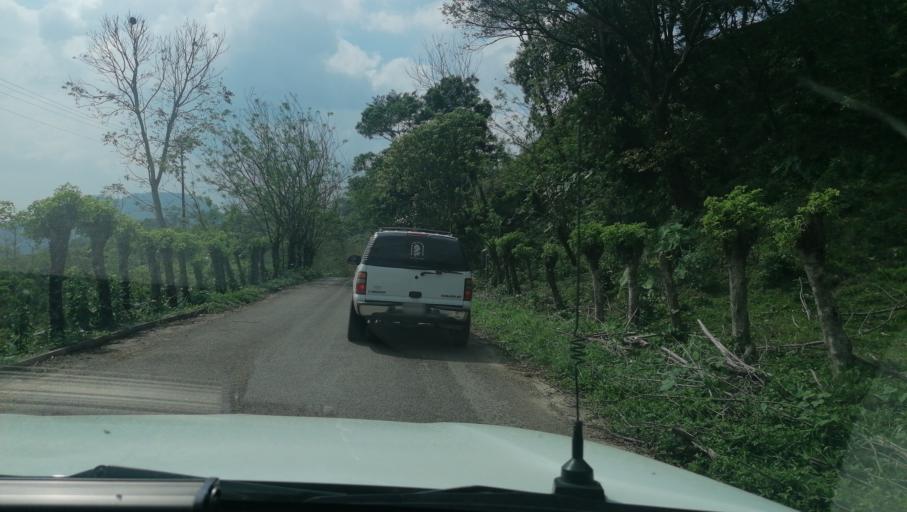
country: MX
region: Chiapas
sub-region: Francisco Leon
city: San Miguel la Sardina
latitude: 17.2341
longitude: -93.3363
